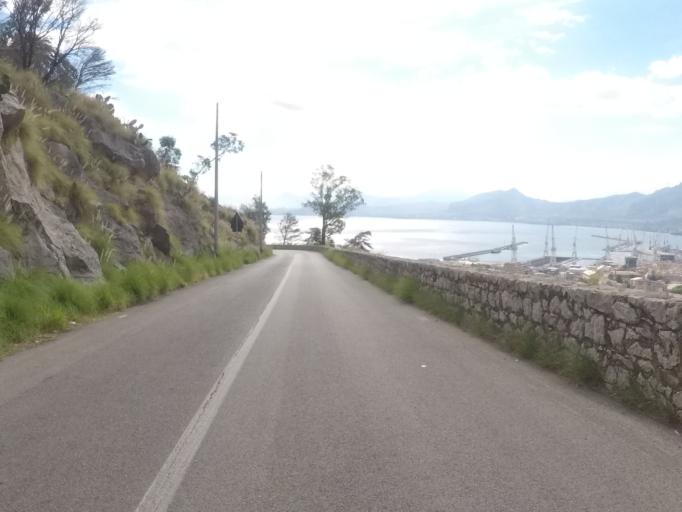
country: IT
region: Sicily
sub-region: Palermo
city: Palermo
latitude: 38.1520
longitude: 13.3619
